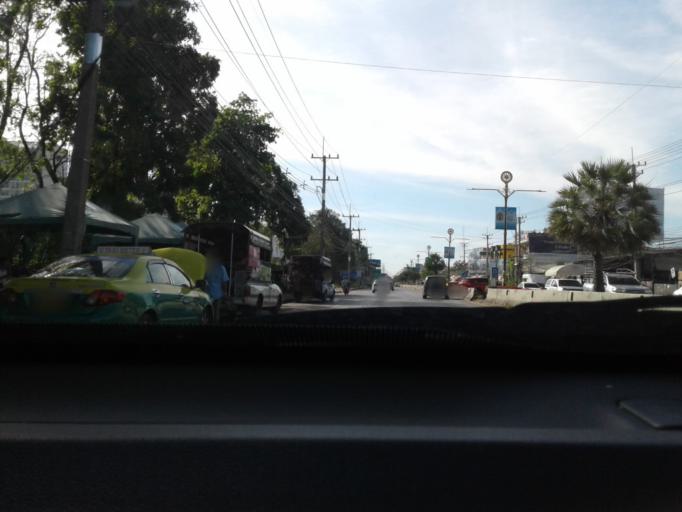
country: TH
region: Nakhon Pathom
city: Salaya
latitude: 13.8011
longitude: 100.3249
